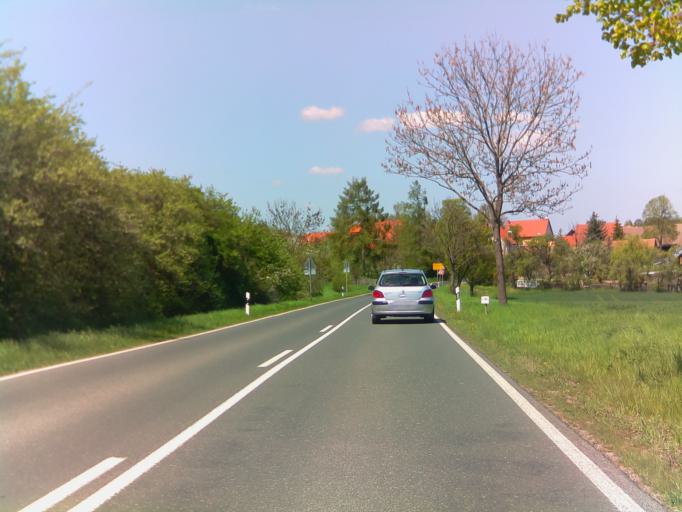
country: DE
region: Thuringia
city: Behringen
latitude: 50.7941
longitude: 10.9836
